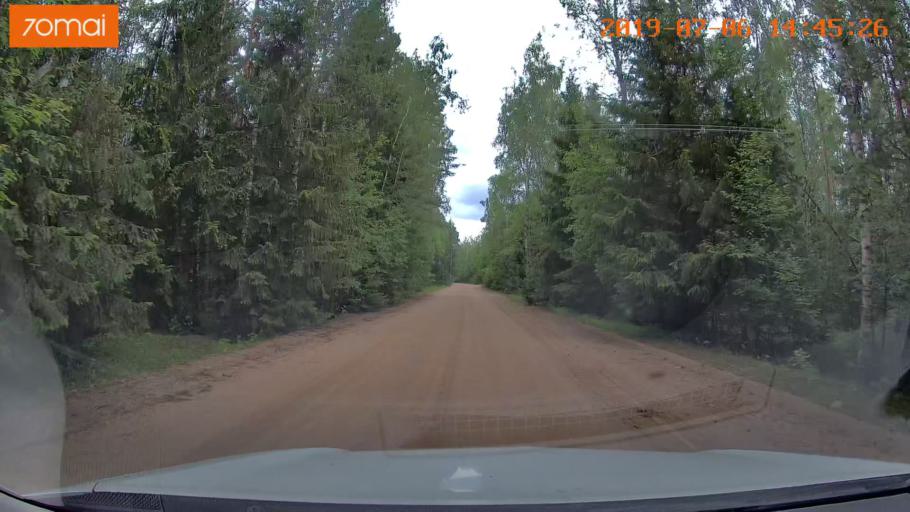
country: BY
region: Minsk
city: Ivyanyets
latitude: 53.9719
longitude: 26.6869
